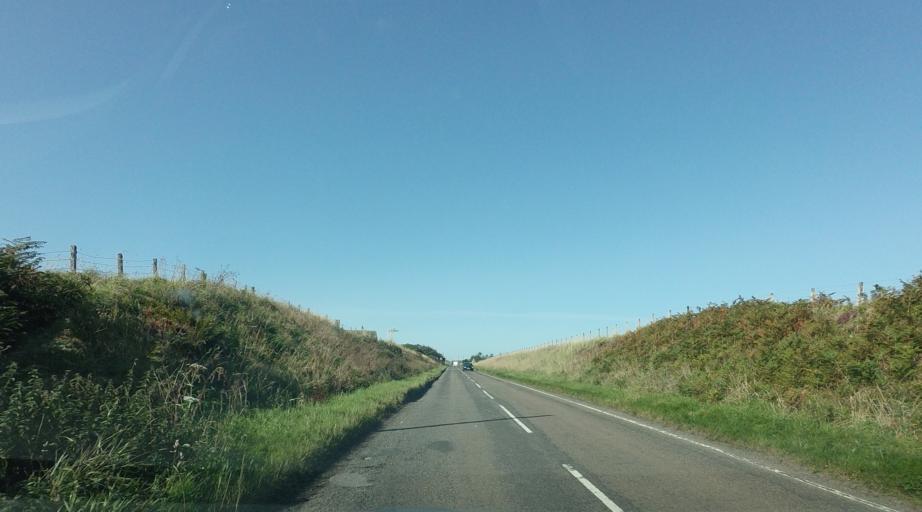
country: GB
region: Scotland
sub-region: Highland
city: Wick
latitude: 58.6368
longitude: -3.1656
